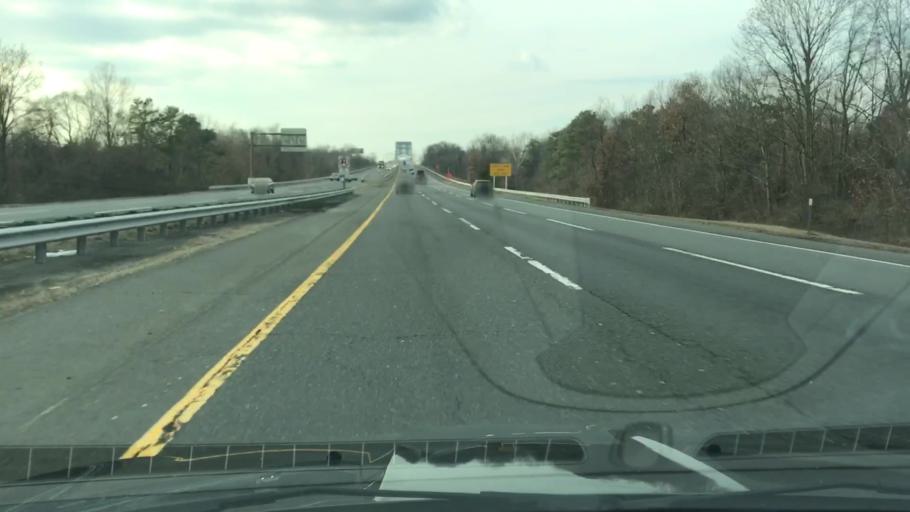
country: US
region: Pennsylvania
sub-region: Bucks County
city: Tullytown
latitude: 40.1123
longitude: -74.8135
